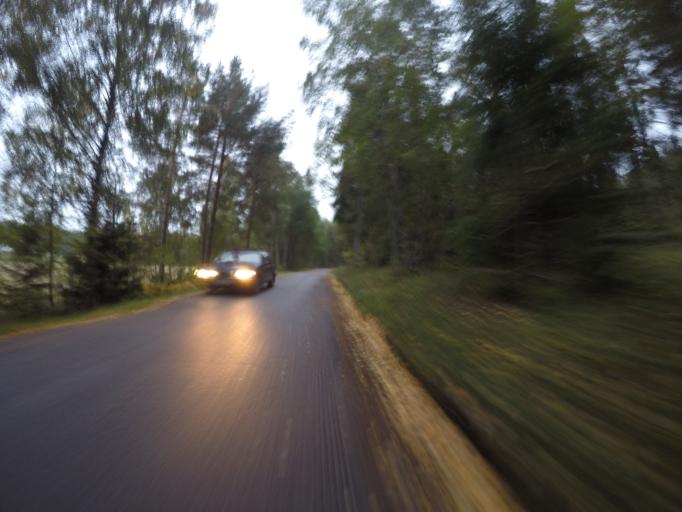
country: SE
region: Vaestmanland
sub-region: Kungsors Kommun
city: Kungsoer
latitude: 59.4111
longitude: 16.1105
